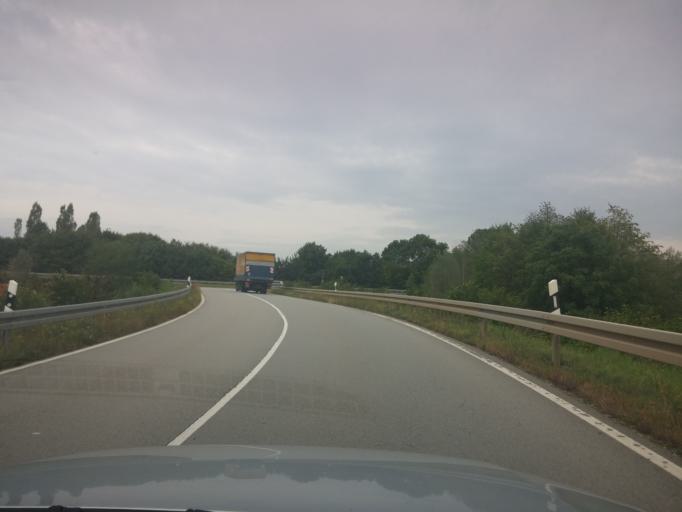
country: DE
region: Bavaria
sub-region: Upper Bavaria
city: Feldkirchen
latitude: 48.1666
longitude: 11.7358
